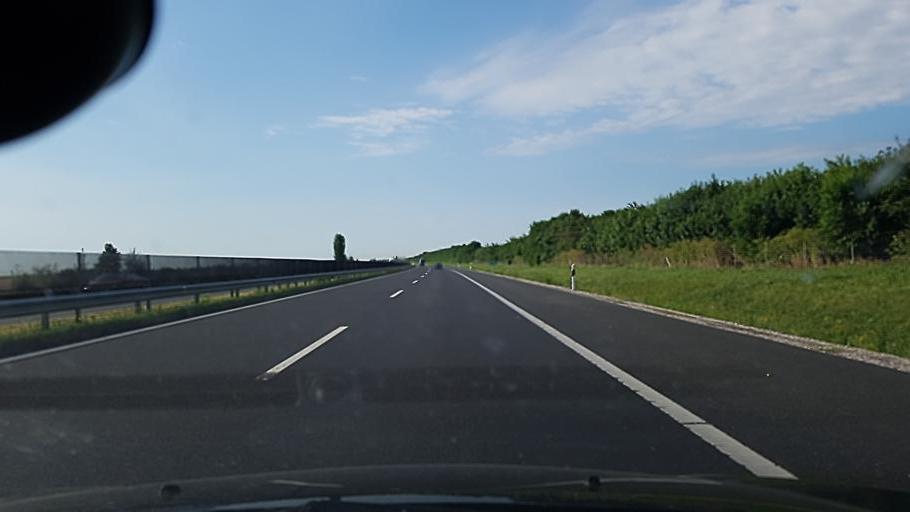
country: HU
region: Fejer
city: Ivancsa
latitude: 47.1486
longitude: 18.8058
